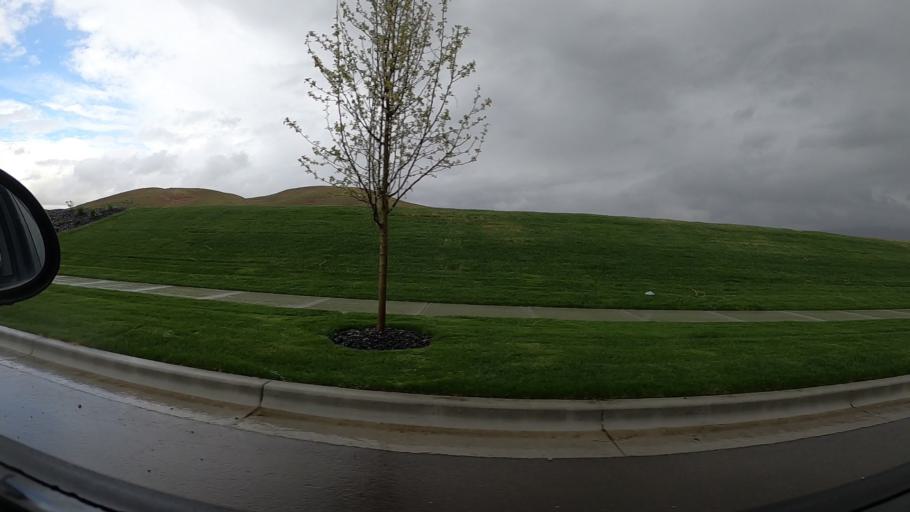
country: US
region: Idaho
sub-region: Ada County
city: Eagle
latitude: 43.7355
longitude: -116.2837
